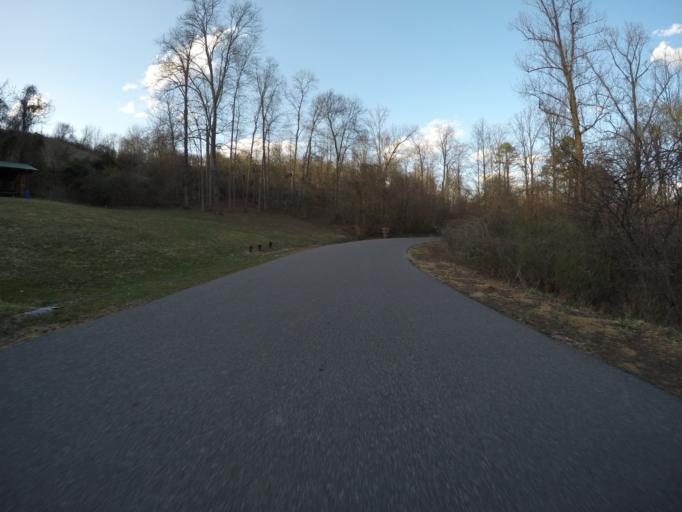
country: US
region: West Virginia
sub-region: Kanawha County
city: Charleston
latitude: 38.3894
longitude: -81.5731
